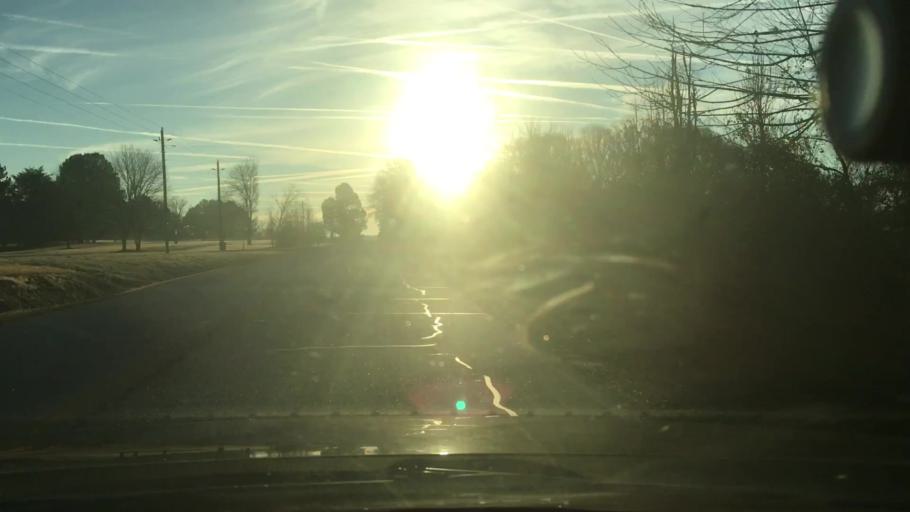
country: US
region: Georgia
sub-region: Coweta County
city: Senoia
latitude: 33.3239
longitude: -84.4923
